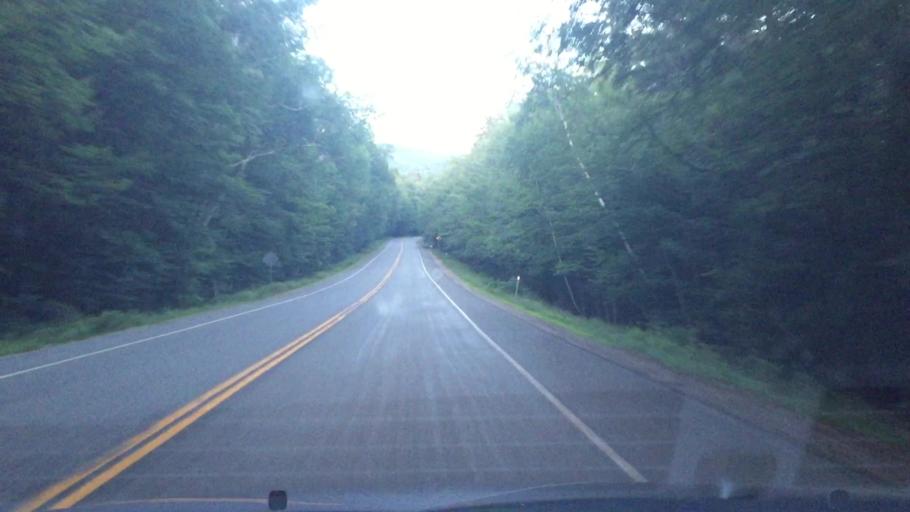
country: US
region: New Hampshire
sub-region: Grafton County
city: Woodstock
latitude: 44.0527
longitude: -71.5788
